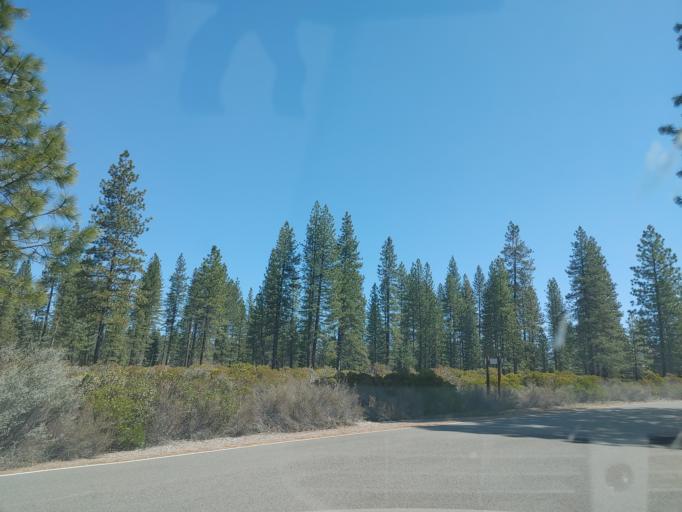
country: US
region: California
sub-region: Siskiyou County
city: McCloud
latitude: 41.2447
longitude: -122.0093
